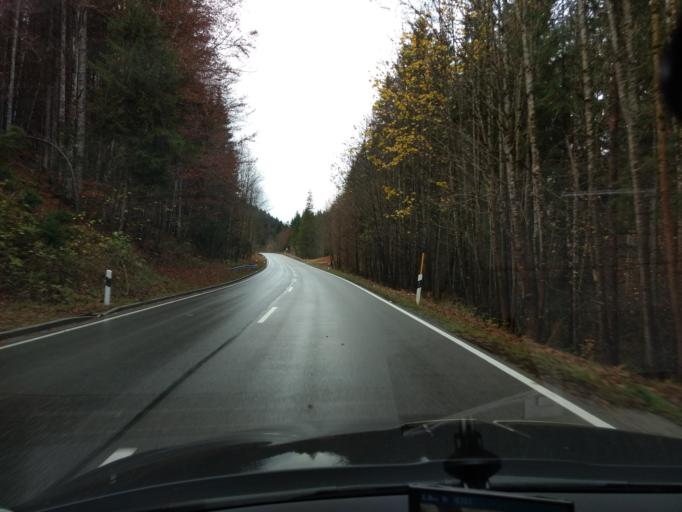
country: DE
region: Bavaria
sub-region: Upper Bavaria
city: Jachenau
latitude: 47.5613
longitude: 11.5139
